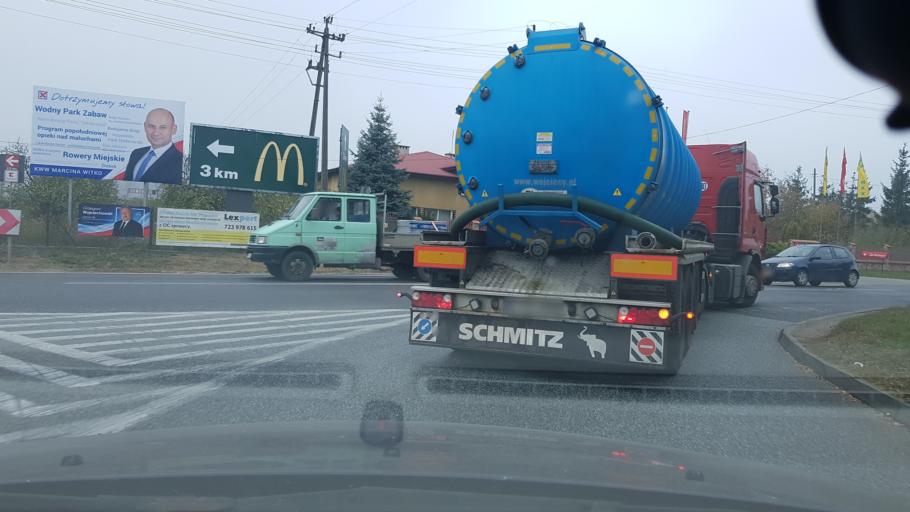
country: PL
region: Lodz Voivodeship
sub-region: Powiat tomaszowski
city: Tomaszow Mazowiecki
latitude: 51.5566
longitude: 20.0193
